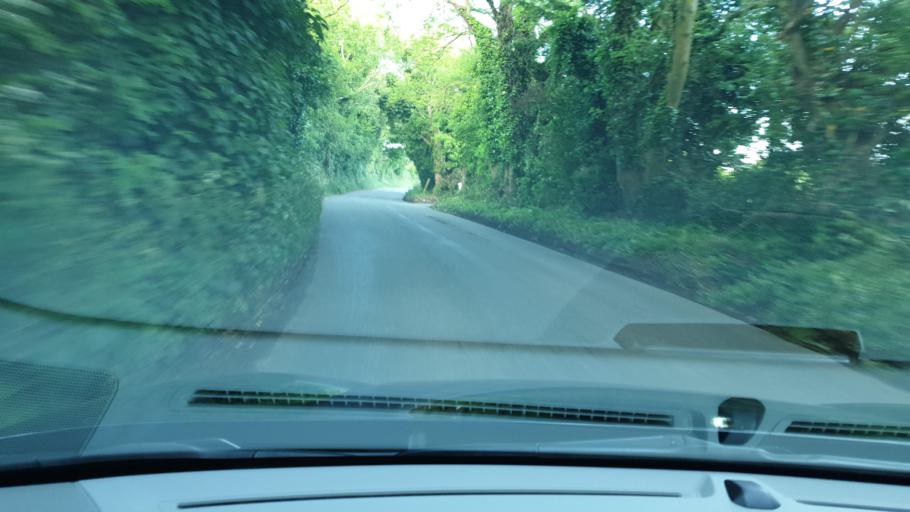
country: IE
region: Leinster
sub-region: An Mhi
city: Ashbourne
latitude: 53.5614
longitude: -6.3929
